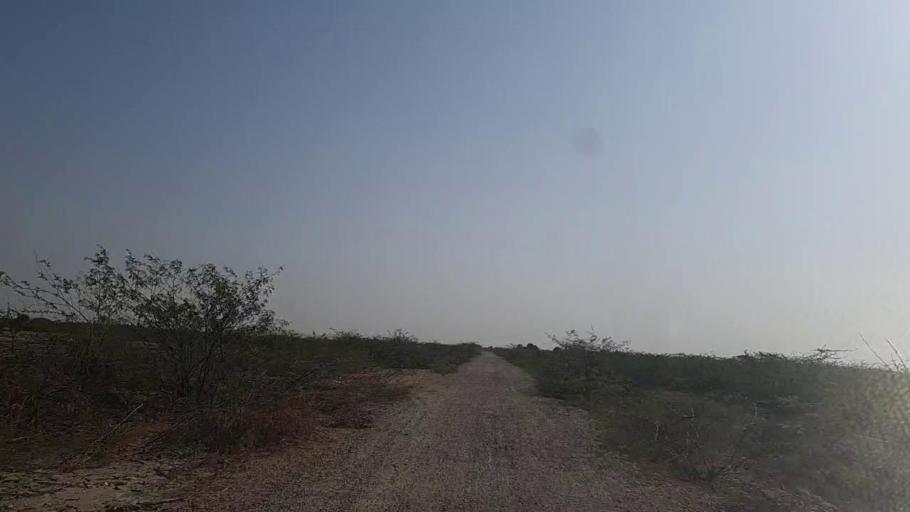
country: PK
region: Sindh
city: Naukot
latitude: 24.5962
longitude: 69.2634
